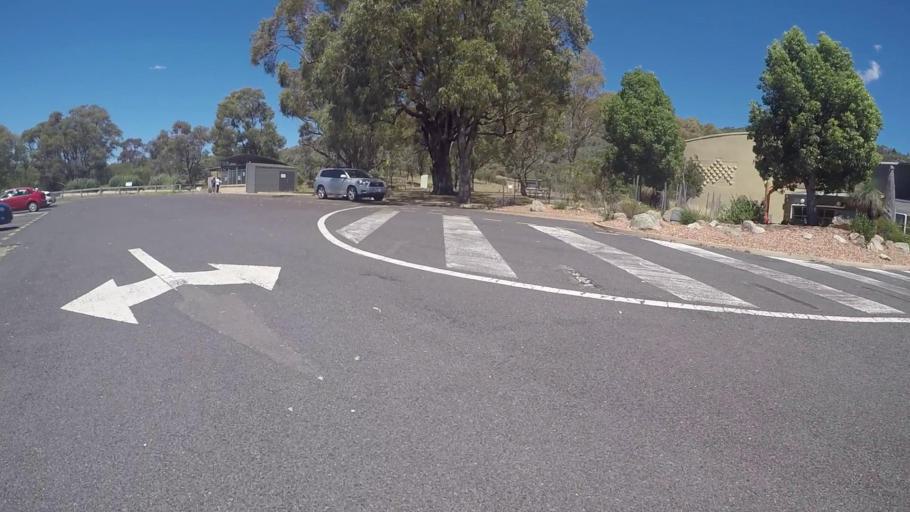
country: AU
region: Australian Capital Territory
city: Macarthur
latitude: -35.4400
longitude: 148.9429
